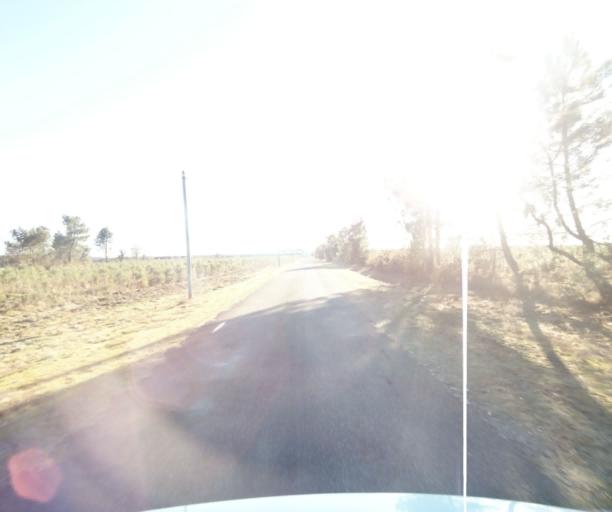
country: FR
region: Aquitaine
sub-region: Departement des Landes
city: Gabarret
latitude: 44.1324
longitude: -0.0933
